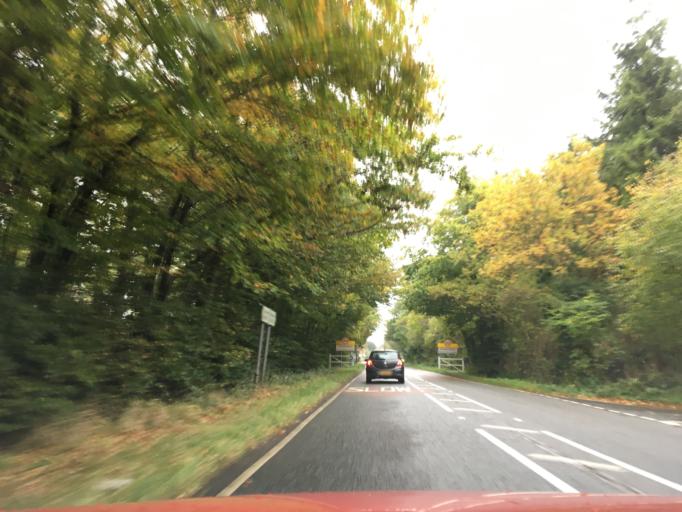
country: GB
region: England
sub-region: West Berkshire
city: Winterbourne
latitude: 51.4168
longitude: -1.3812
